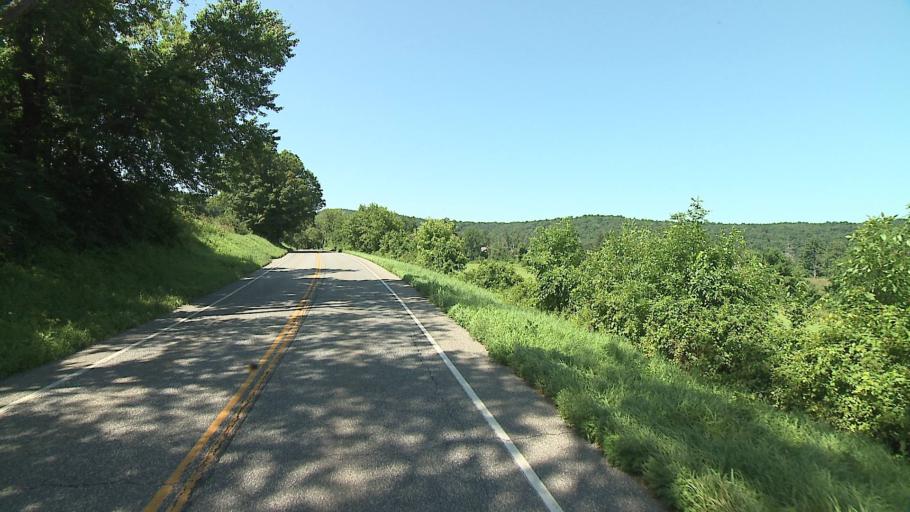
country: US
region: Connecticut
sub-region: Litchfield County
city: Kent
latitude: 41.8748
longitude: -73.4929
